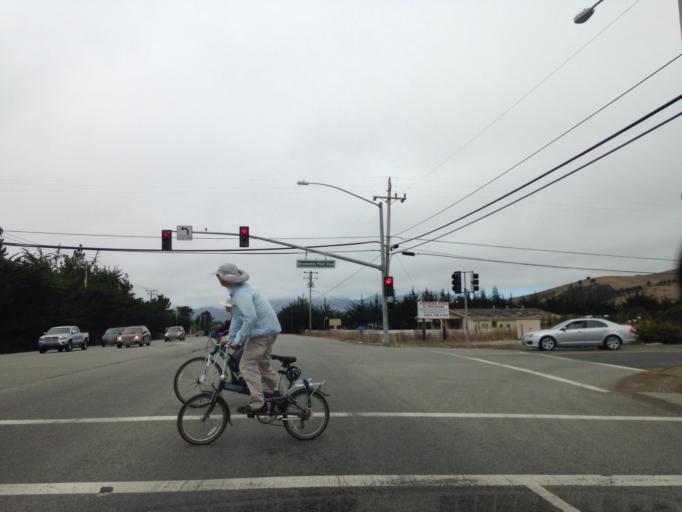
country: US
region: California
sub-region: San Mateo County
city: Half Moon Bay
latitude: 37.4310
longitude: -122.4266
